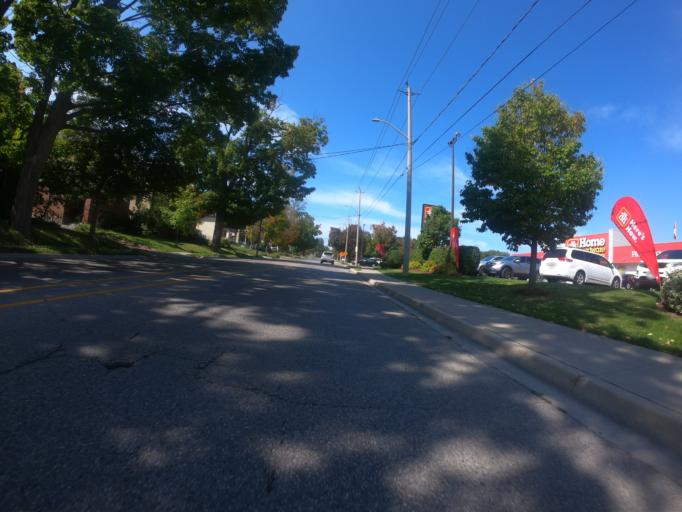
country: CA
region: Ontario
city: Waterloo
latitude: 43.4499
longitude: -80.5049
